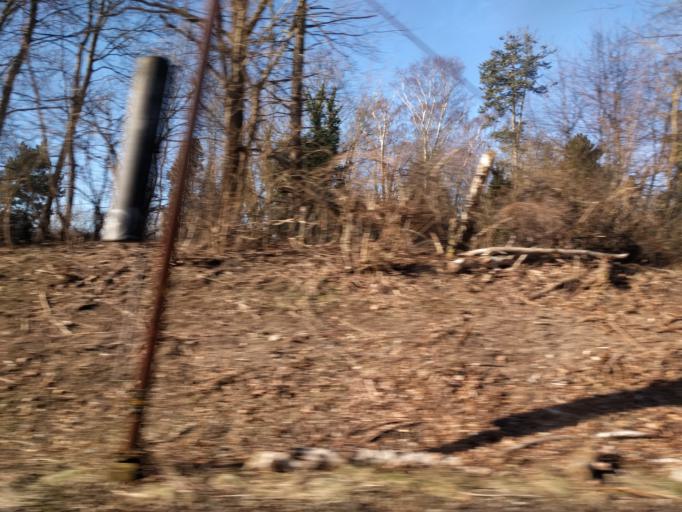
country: DK
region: Capital Region
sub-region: Rudersdal Kommune
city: Trorod
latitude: 55.8563
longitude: 12.5572
